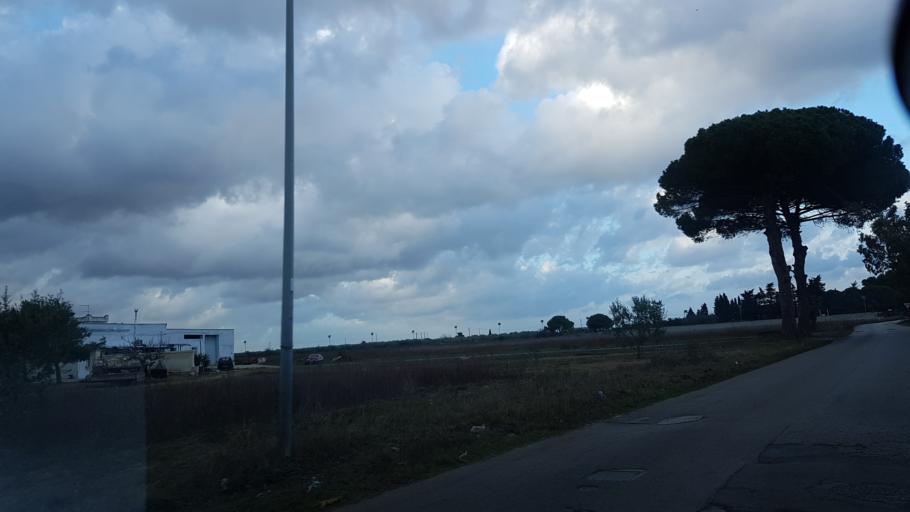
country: IT
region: Apulia
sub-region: Provincia di Brindisi
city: San Pietro Vernotico
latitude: 40.4968
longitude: 18.0026
